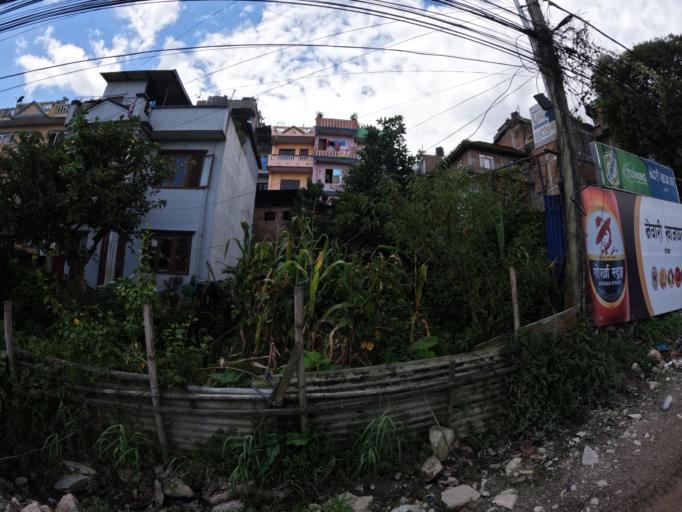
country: NP
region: Central Region
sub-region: Bagmati Zone
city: Kathmandu
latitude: 27.7665
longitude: 85.3301
